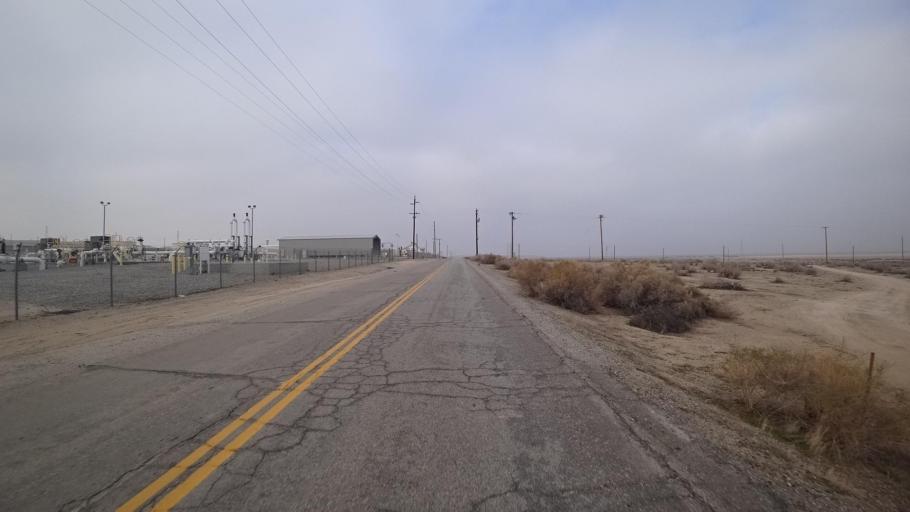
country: US
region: California
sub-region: Kern County
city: Maricopa
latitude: 35.1520
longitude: -119.3360
